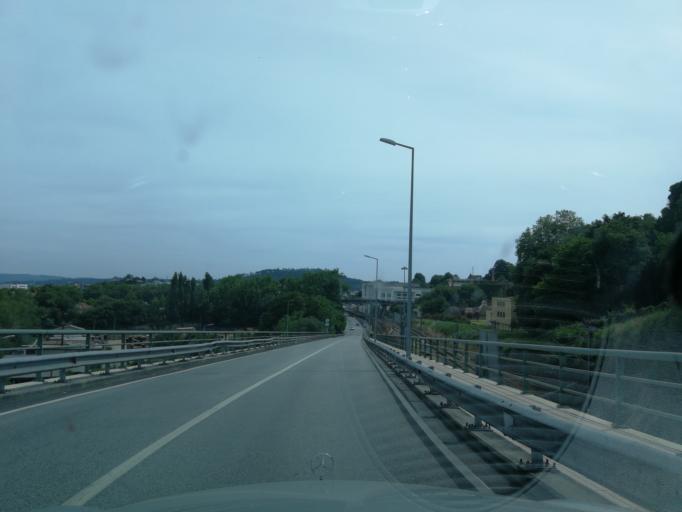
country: PT
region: Braga
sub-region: Vila Nova de Famalicao
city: Calendario
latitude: 41.4105
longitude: -8.5269
